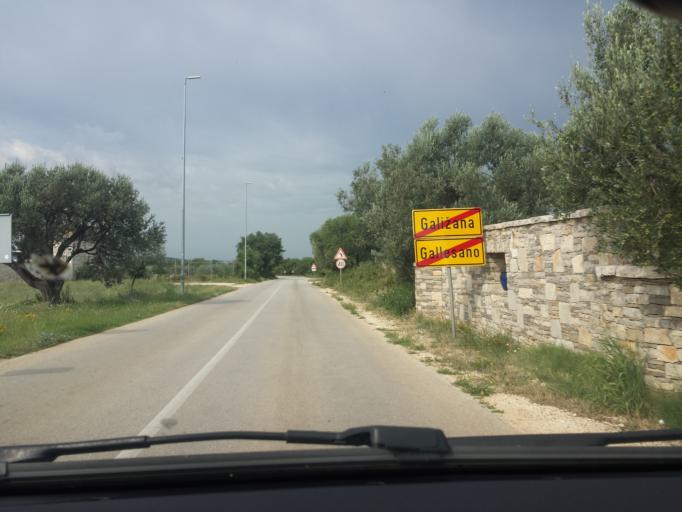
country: HR
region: Istarska
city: Galizana
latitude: 44.9242
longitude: 13.8634
